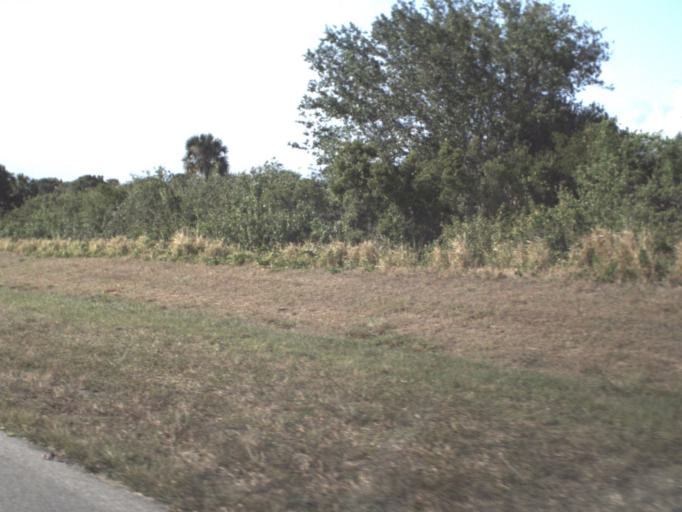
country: US
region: Florida
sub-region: Brevard County
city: Melbourne
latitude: 28.1080
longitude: -80.6299
